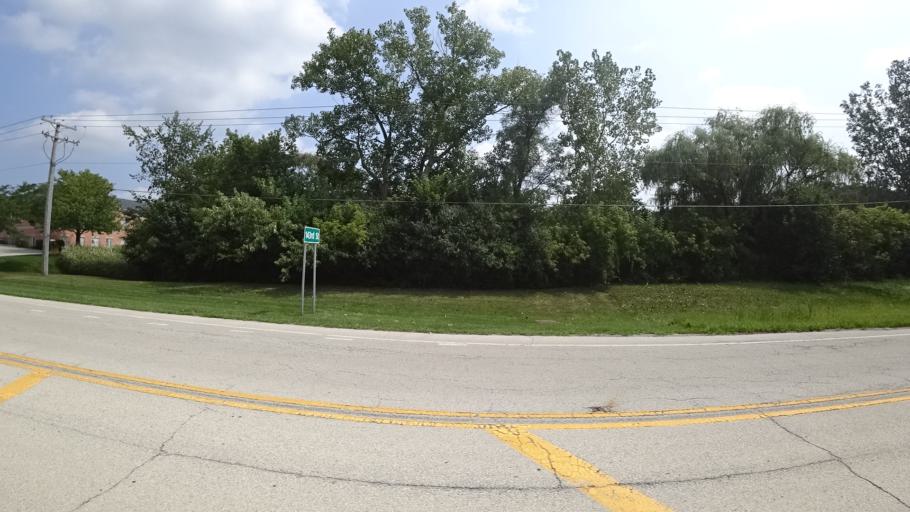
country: US
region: Illinois
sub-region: Cook County
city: Orland Park
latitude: 41.6287
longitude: -87.8827
